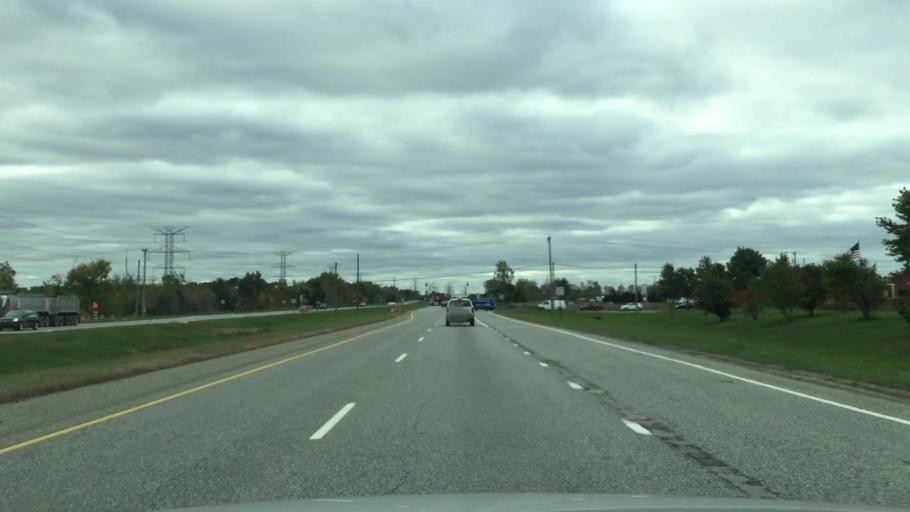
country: US
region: Michigan
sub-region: Macomb County
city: Romeo
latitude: 42.7742
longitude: -83.0095
